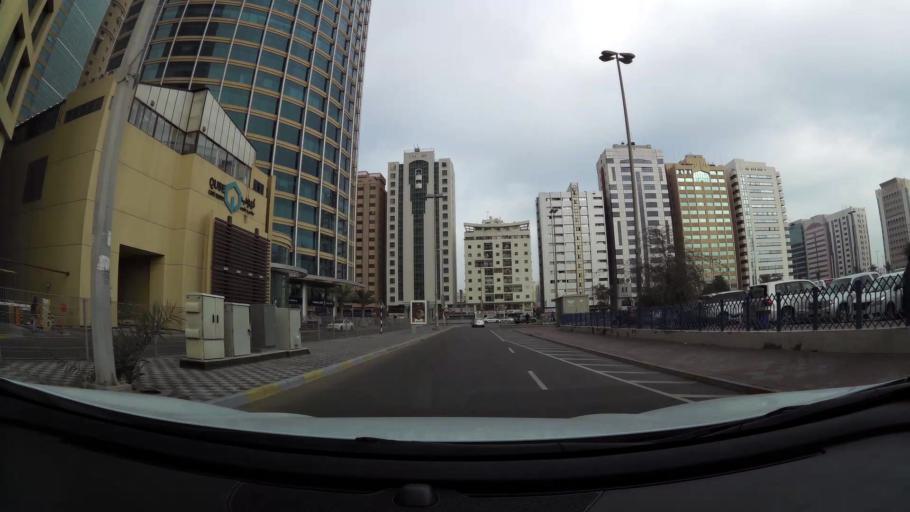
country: AE
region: Abu Dhabi
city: Abu Dhabi
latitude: 24.4718
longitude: 54.3747
